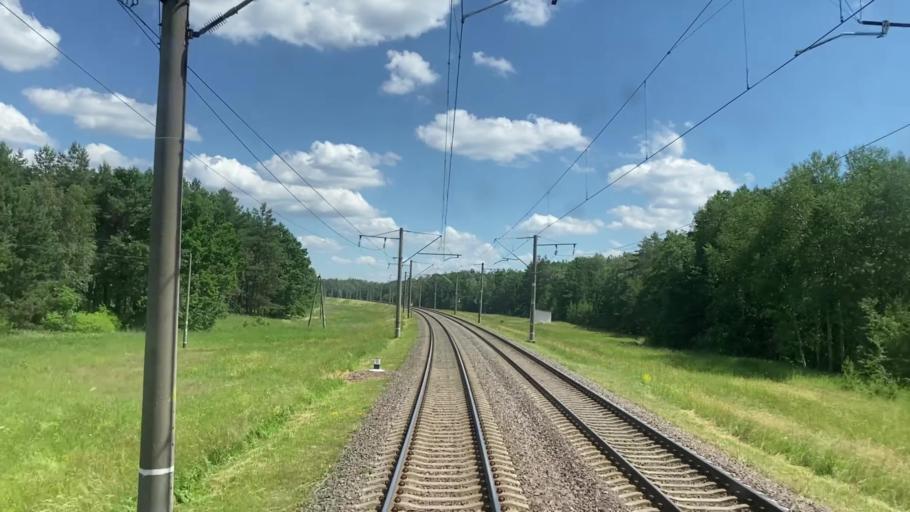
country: BY
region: Brest
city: Ivatsevichy
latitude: 52.8436
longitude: 25.5561
